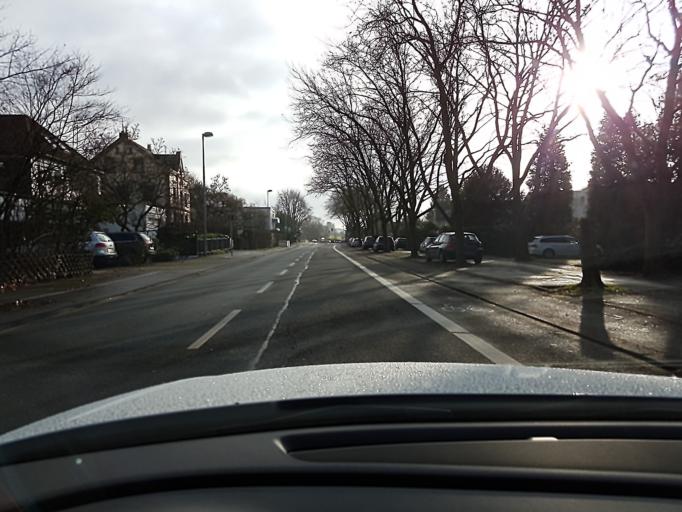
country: DE
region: North Rhine-Westphalia
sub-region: Regierungsbezirk Dusseldorf
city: Muelheim (Ruhr)
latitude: 51.4059
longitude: 6.8969
